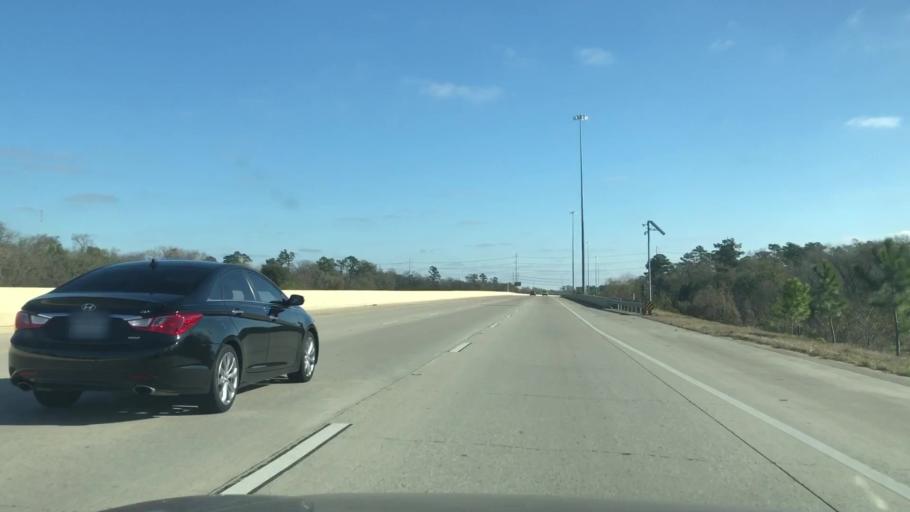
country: US
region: Texas
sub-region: Harris County
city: Jacinto City
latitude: 29.7881
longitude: -95.2407
